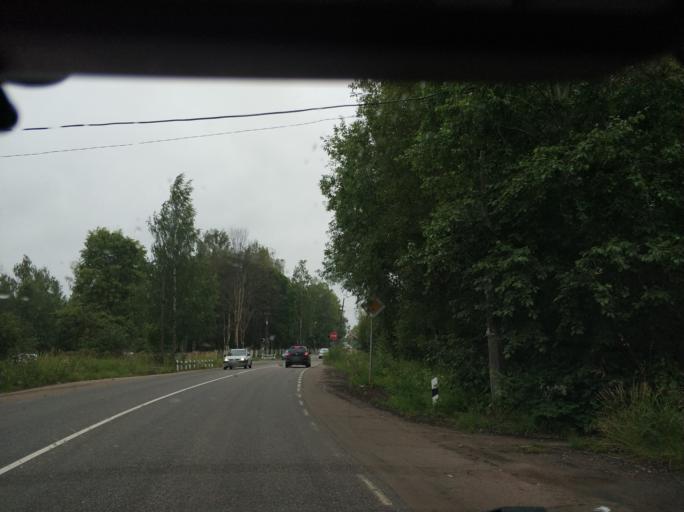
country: RU
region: Leningrad
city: Imeni Morozova
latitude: 59.9757
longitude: 31.0254
